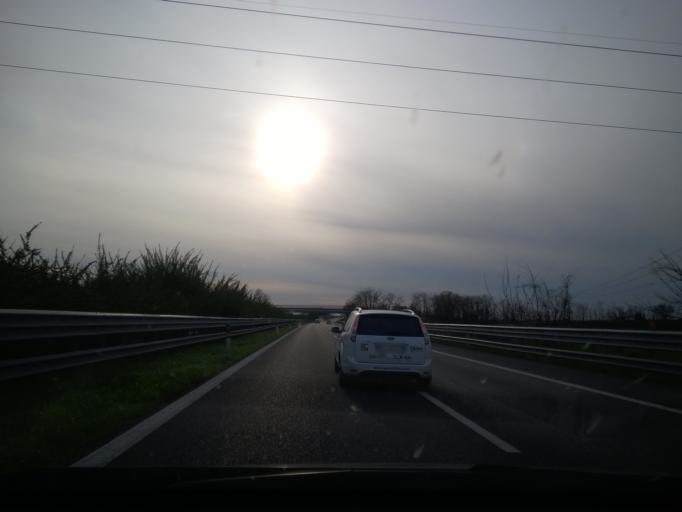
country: IT
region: Emilia-Romagna
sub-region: Provincia di Piacenza
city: Monticelli d'Ongina
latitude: 45.0582
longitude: 9.9194
